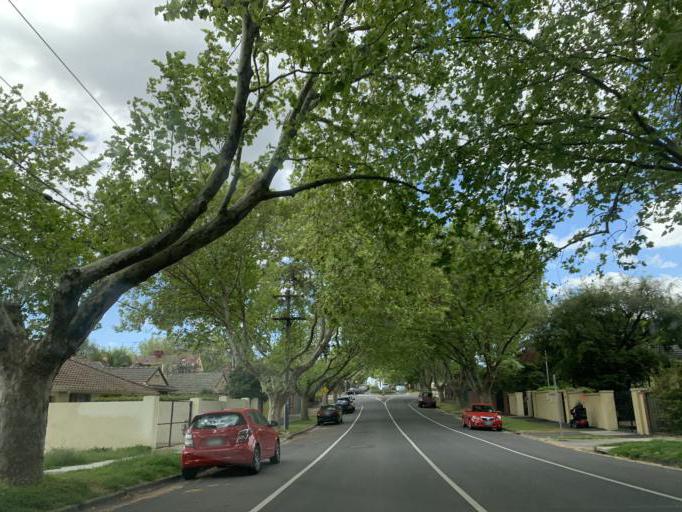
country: AU
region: Victoria
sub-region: Bayside
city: North Brighton
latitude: -37.9195
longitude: 144.9971
